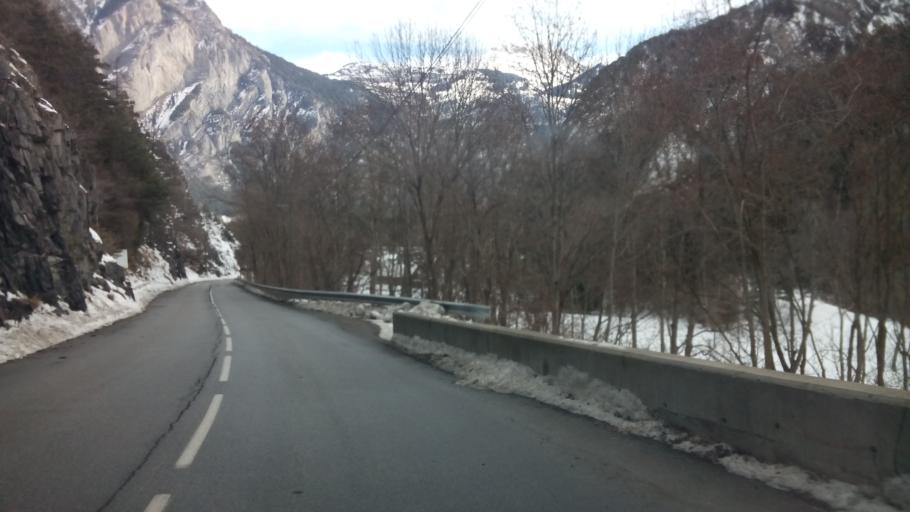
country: FR
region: Rhone-Alpes
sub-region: Departement de l'Isere
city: Huez
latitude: 45.0716
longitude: 6.0073
